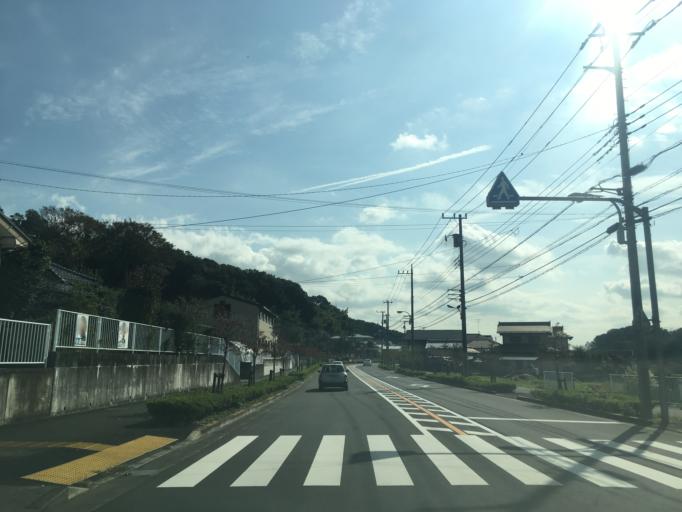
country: JP
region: Tokyo
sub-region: Machida-shi
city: Machida
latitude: 35.5939
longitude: 139.4139
